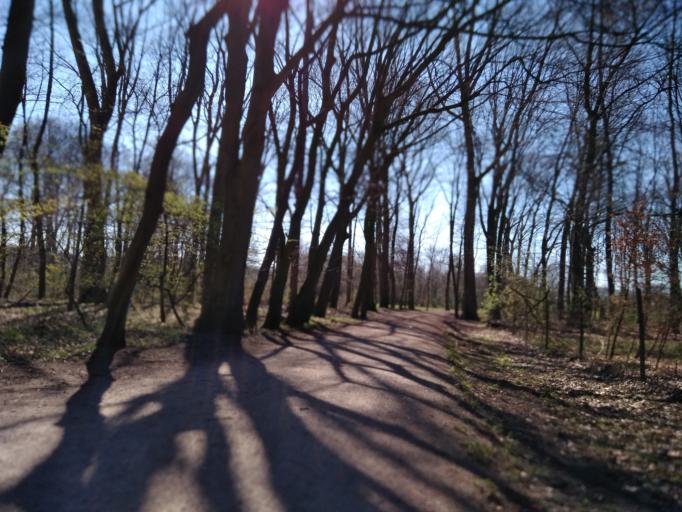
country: DE
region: North Rhine-Westphalia
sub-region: Regierungsbezirk Munster
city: Gladbeck
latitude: 51.6136
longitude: 7.0367
